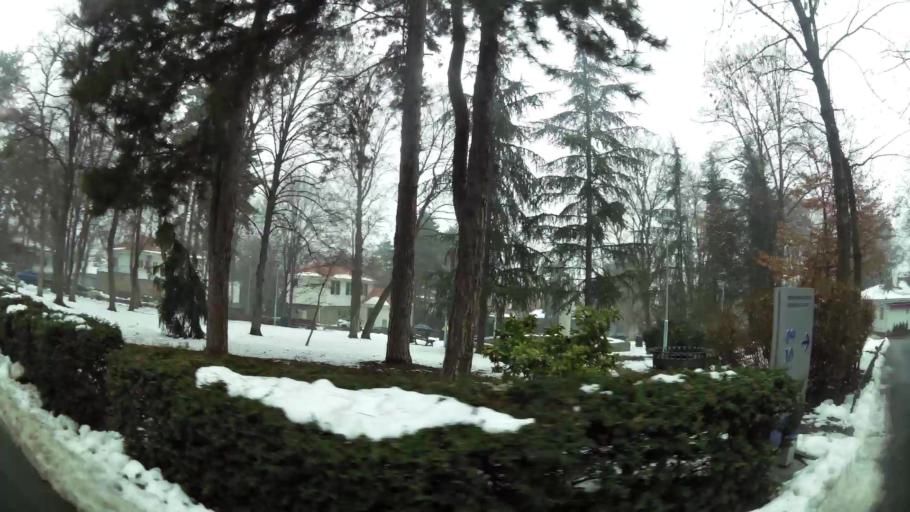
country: RS
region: Central Serbia
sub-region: Belgrade
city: Savski Venac
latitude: 44.7780
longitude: 20.4632
